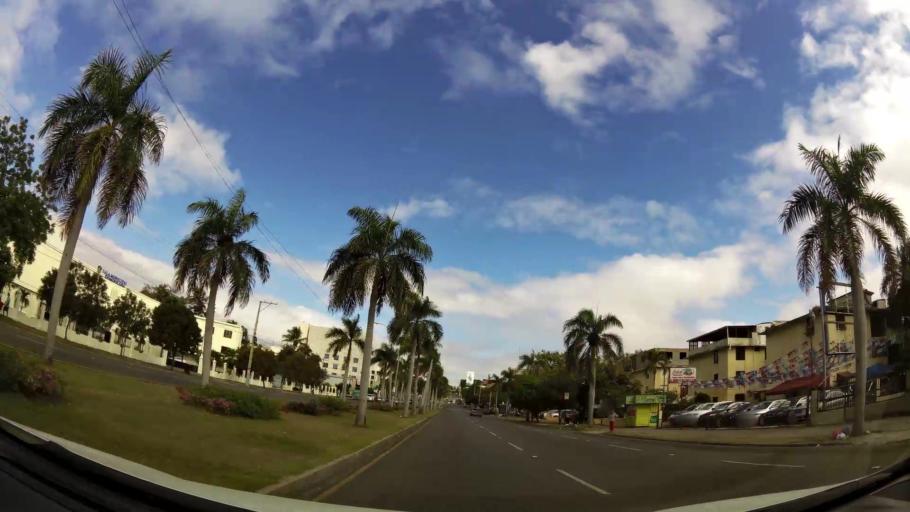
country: DO
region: Nacional
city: La Julia
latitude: 18.4521
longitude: -69.9282
